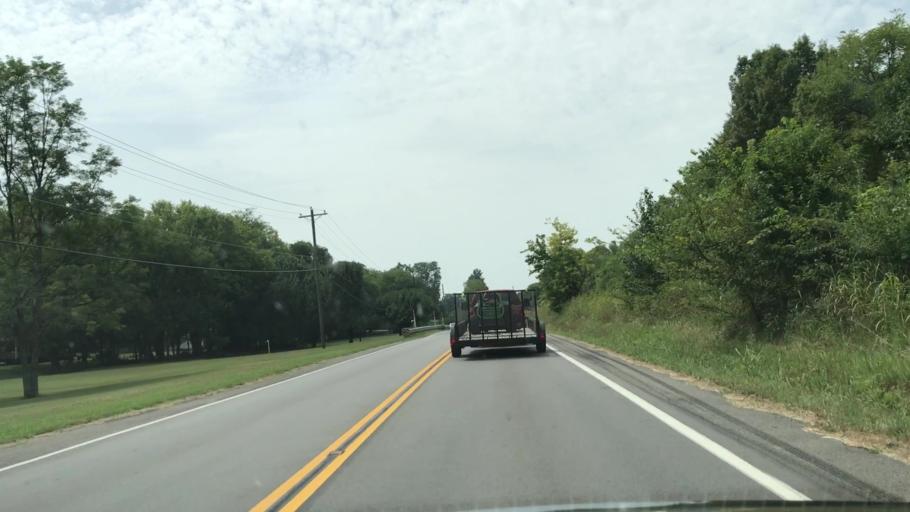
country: US
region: Tennessee
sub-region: Williamson County
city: Brentwood Estates
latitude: 35.9306
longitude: -86.7676
